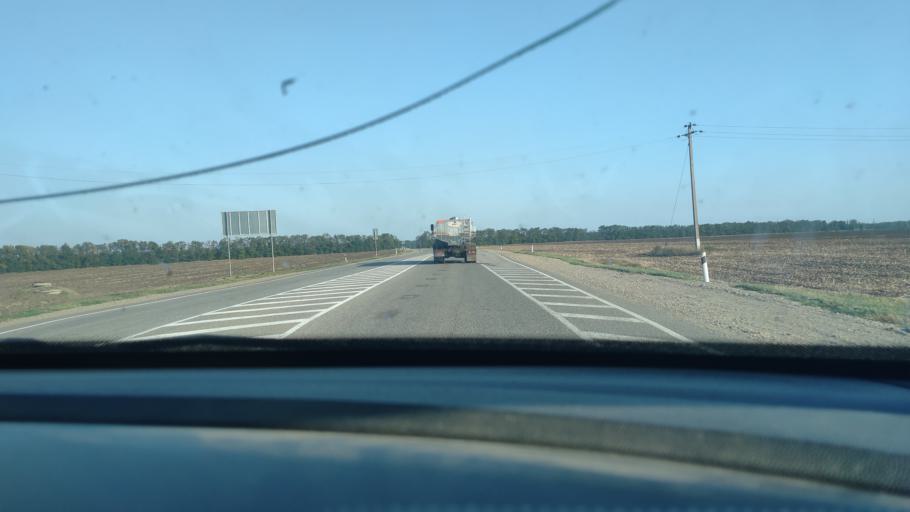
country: RU
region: Krasnodarskiy
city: Starominskaya
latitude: 46.5023
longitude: 39.0402
